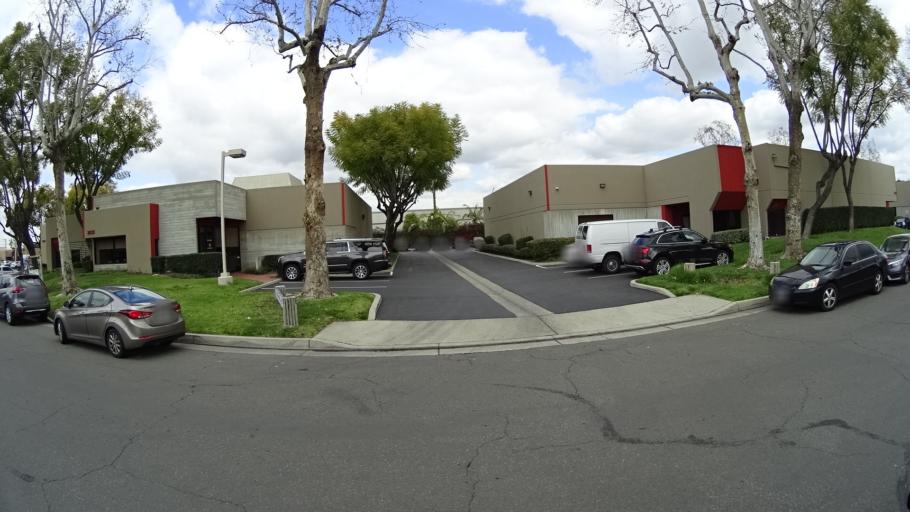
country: US
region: California
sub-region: Orange County
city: Buena Park
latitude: 33.8493
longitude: -117.9733
